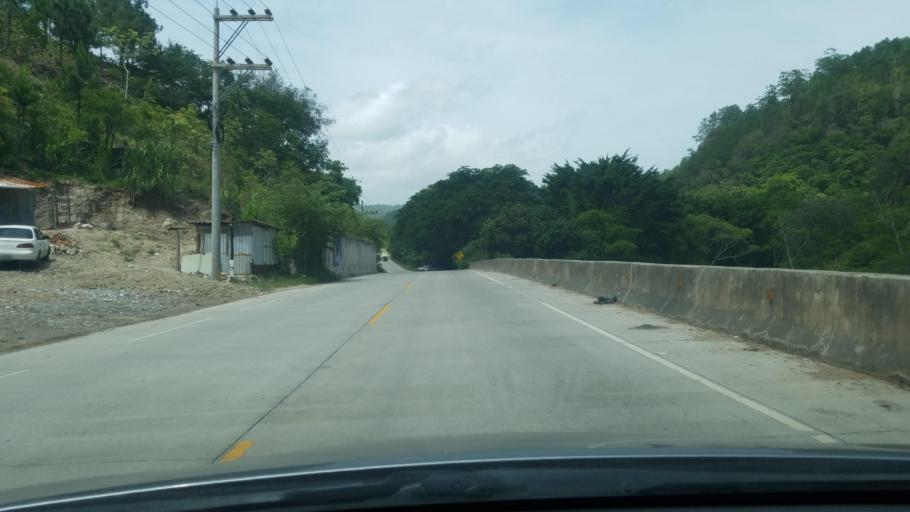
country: HN
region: Copan
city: La Entrada
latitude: 15.0444
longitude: -88.7630
